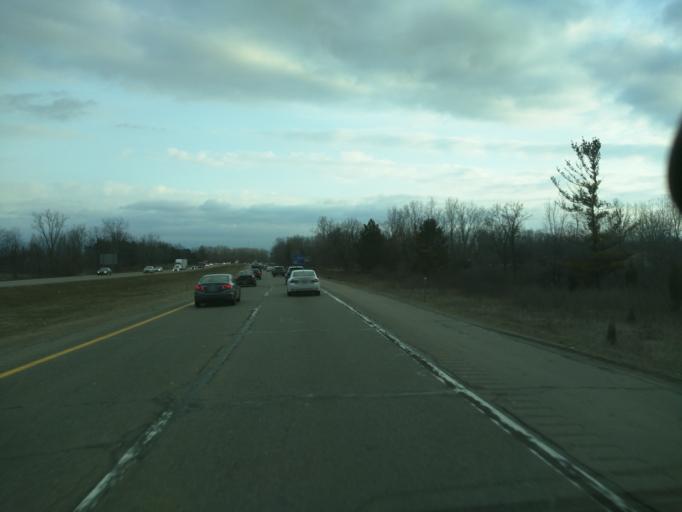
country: US
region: Michigan
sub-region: Ingham County
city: East Lansing
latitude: 42.7025
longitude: -84.5054
